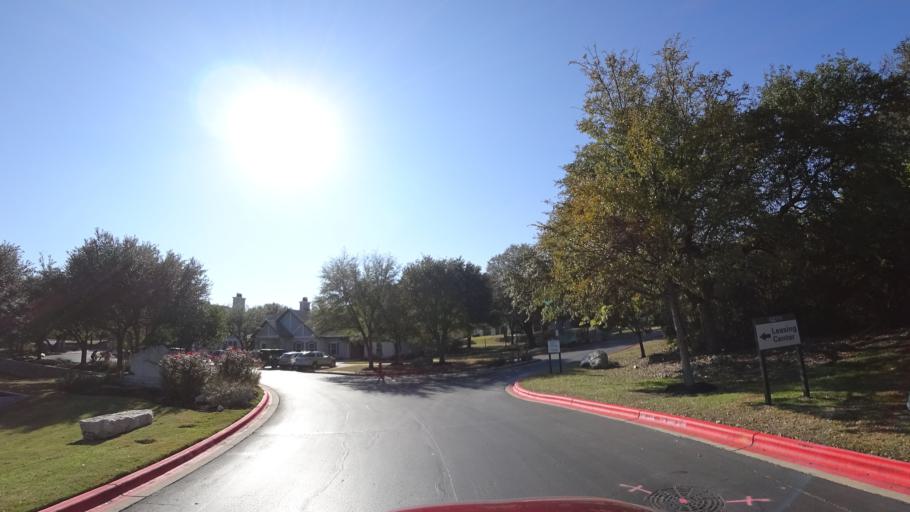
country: US
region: Texas
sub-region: Williamson County
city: Anderson Mill
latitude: 30.3918
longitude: -97.8398
